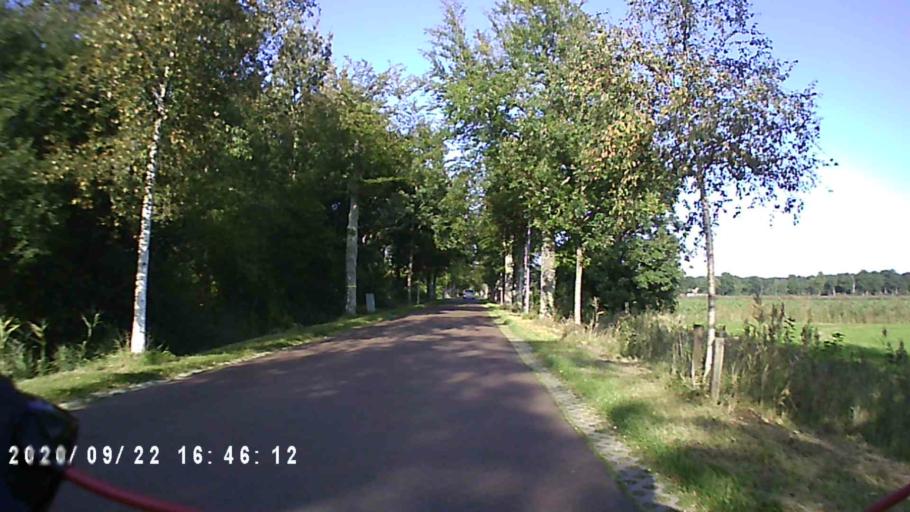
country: NL
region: Groningen
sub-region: Gemeente Leek
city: Leek
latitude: 53.1286
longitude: 6.4703
